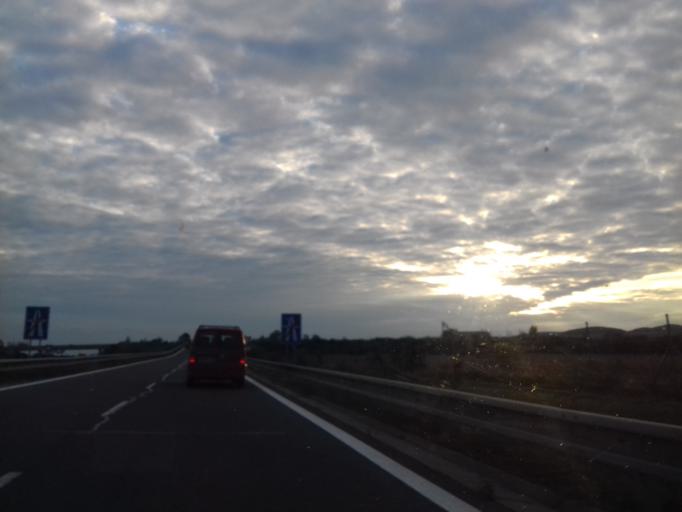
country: SK
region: Trenciansky
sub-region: Okres Trencin
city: Trencin
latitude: 48.8629
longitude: 17.9607
